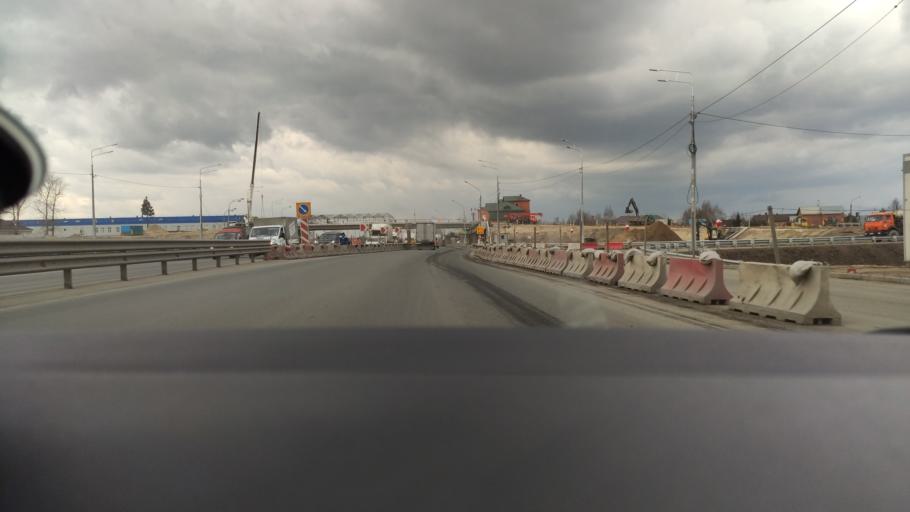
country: RU
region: Moskovskaya
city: Obukhovo
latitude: 55.8288
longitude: 38.2668
